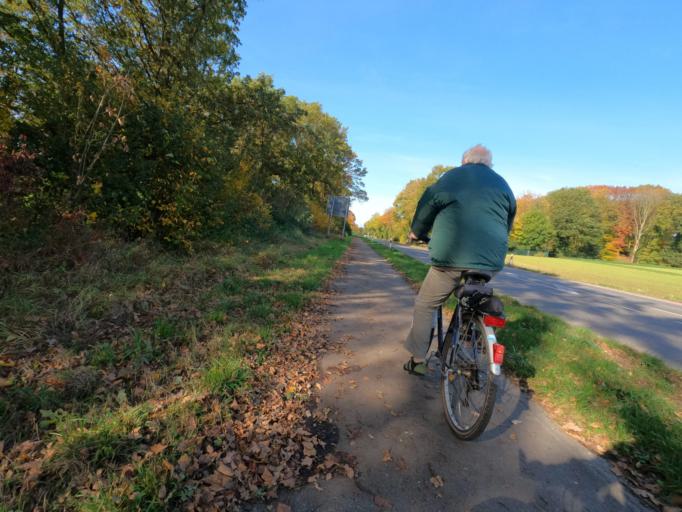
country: DE
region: North Rhine-Westphalia
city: Huckelhoven
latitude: 51.0411
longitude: 6.2558
